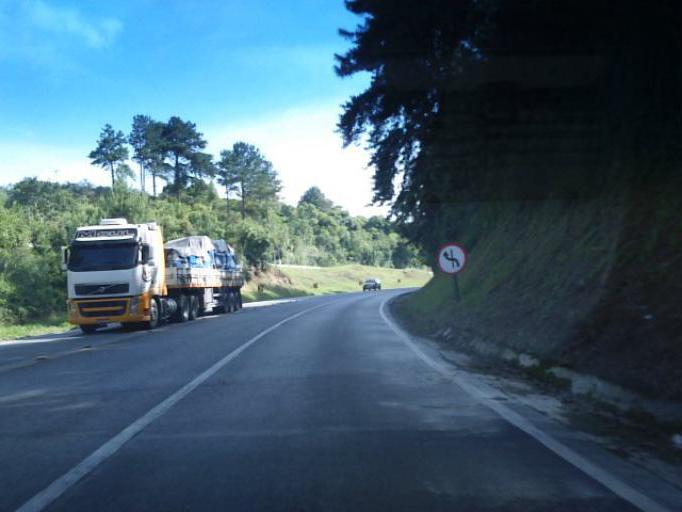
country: BR
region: Parana
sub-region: Campina Grande Do Sul
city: Campina Grande do Sul
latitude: -25.1902
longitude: -48.8847
